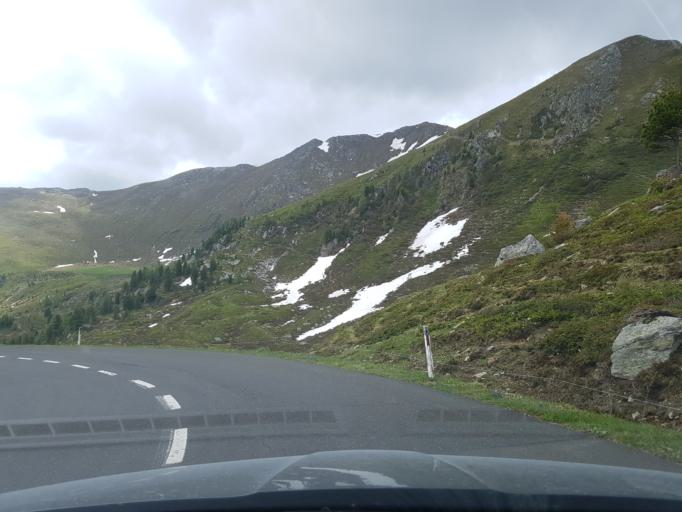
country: AT
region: Carinthia
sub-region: Politischer Bezirk Spittal an der Drau
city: Kleinkirchheim
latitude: 46.8891
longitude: 13.7984
